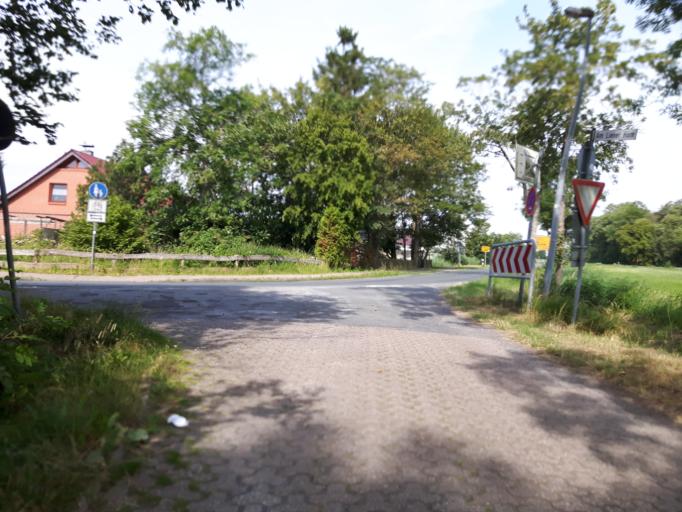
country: DE
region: Lower Saxony
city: Elsfleth
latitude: 53.2548
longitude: 8.4721
